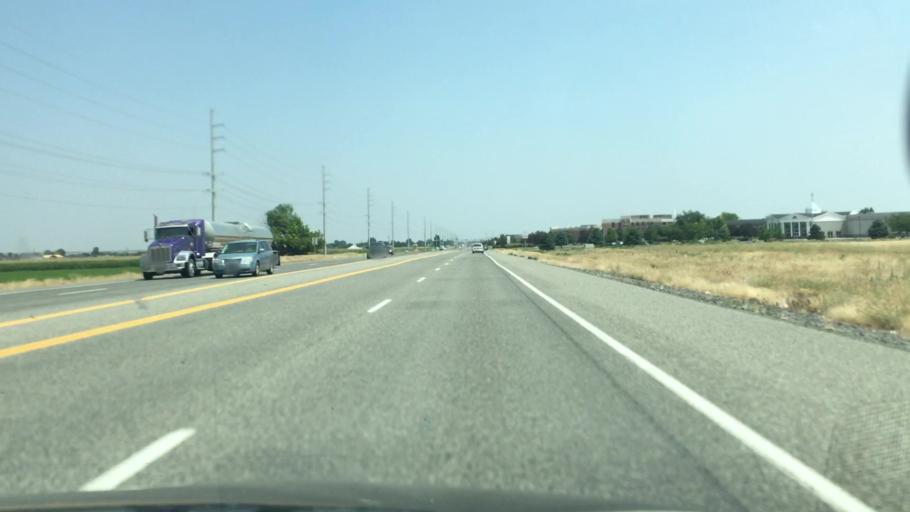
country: US
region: Idaho
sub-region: Twin Falls County
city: Twin Falls
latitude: 42.5916
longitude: -114.5070
